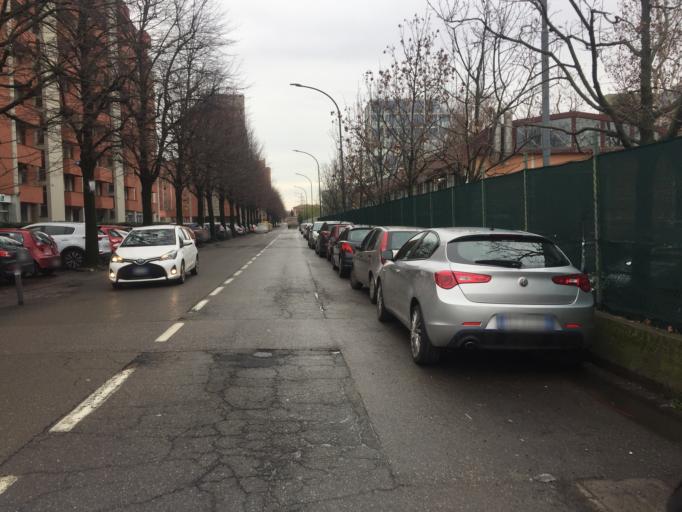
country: IT
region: Emilia-Romagna
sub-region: Provincia di Bologna
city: Casalecchio di Reno
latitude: 44.5035
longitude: 11.2990
